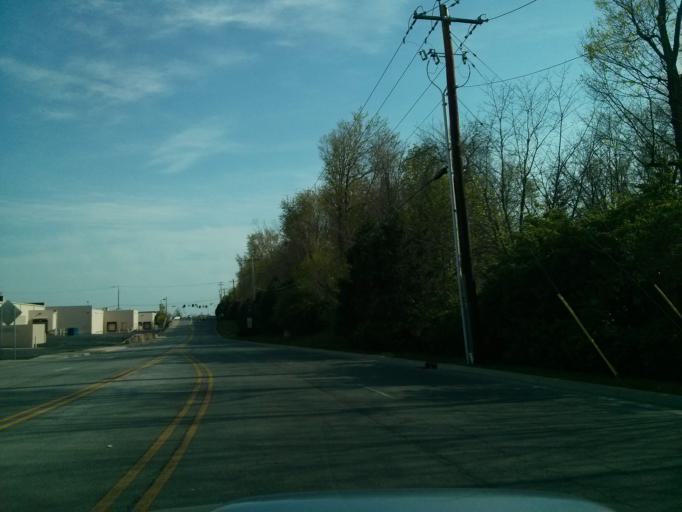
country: US
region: Indiana
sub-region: Hamilton County
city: Carmel
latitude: 40.0031
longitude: -86.1301
